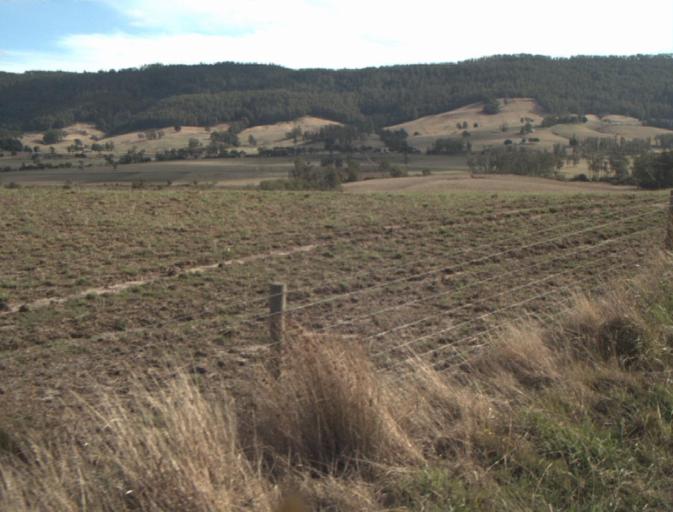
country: AU
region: Tasmania
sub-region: Launceston
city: Mayfield
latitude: -41.2197
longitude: 147.1433
